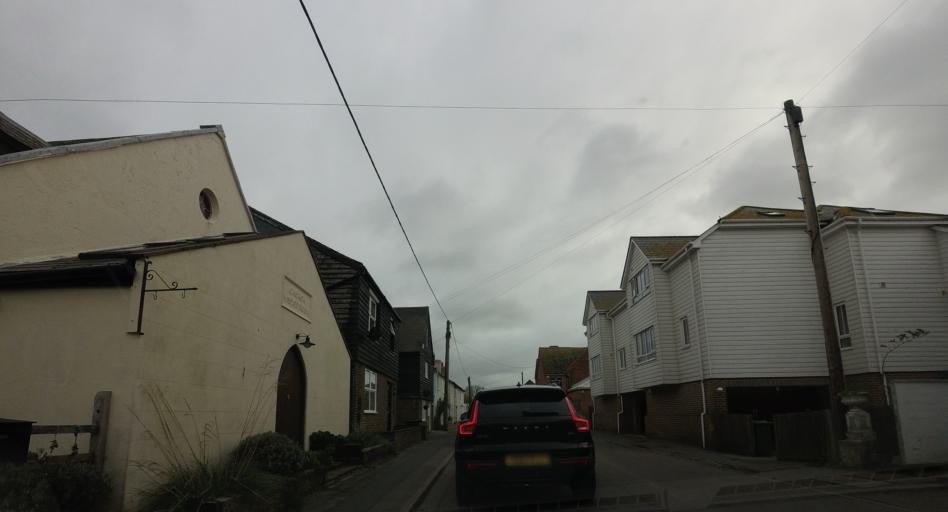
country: GB
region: England
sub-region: East Sussex
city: Rye
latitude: 50.9384
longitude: 0.7605
